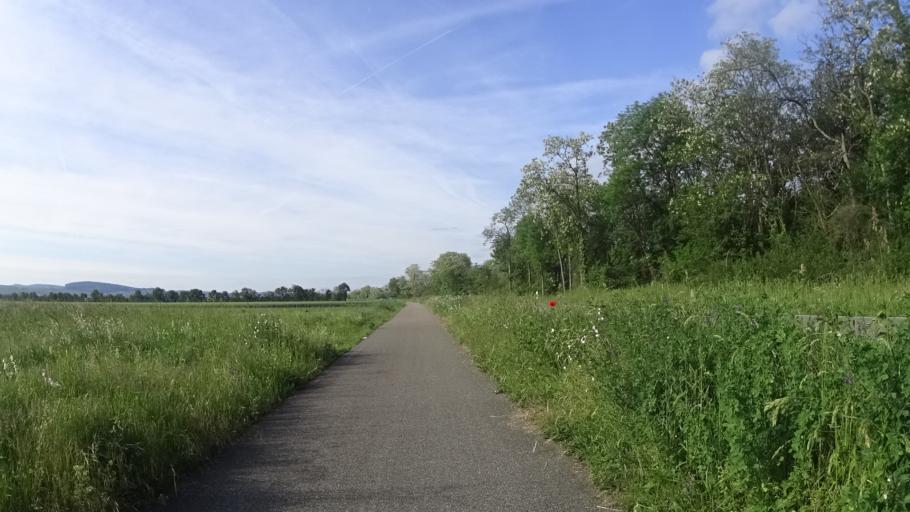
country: DE
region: Baden-Wuerttemberg
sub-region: Freiburg Region
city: Neuenburg am Rhein
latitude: 47.8350
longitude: 7.5748
